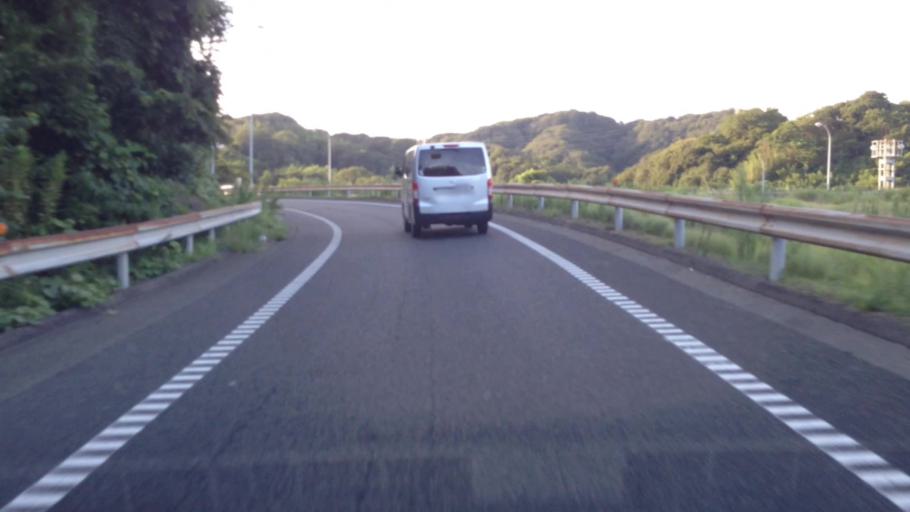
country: JP
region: Kanagawa
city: Yokosuka
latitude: 35.2404
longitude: 139.6591
